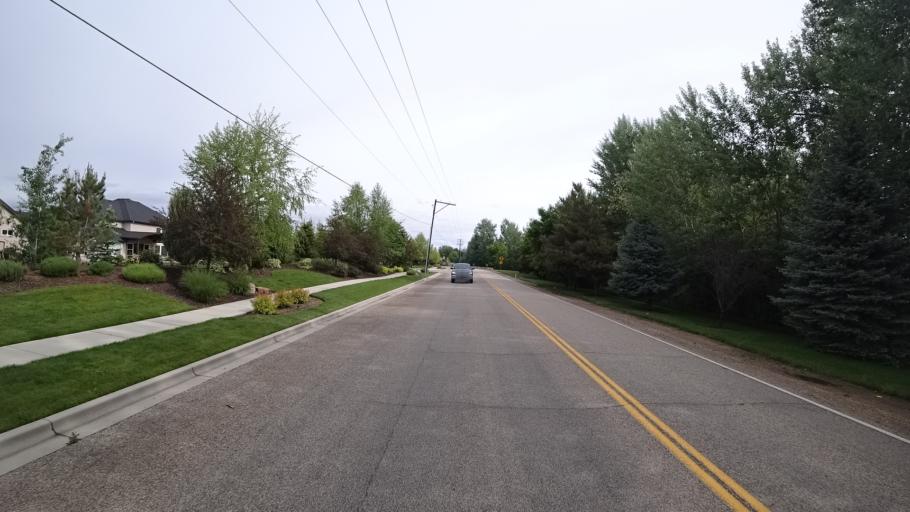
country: US
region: Idaho
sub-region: Ada County
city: Eagle
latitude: 43.7041
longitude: -116.3791
